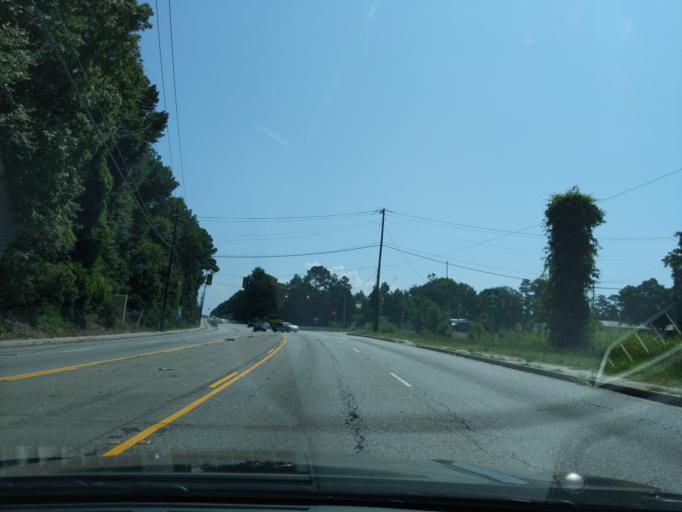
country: US
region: South Carolina
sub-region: Lexington County
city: Oak Grove
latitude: 33.9718
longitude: -81.1385
